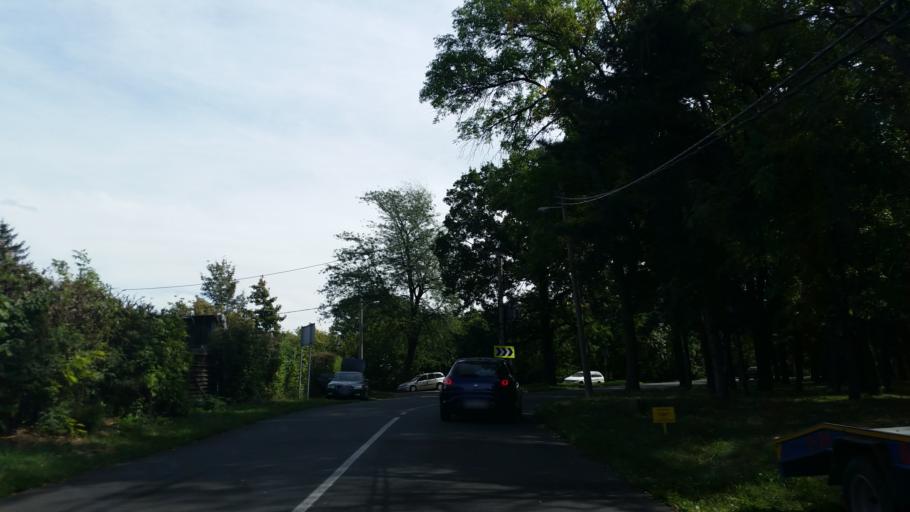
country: RS
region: Central Serbia
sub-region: Belgrade
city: Palilula
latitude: 44.8084
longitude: 20.5046
